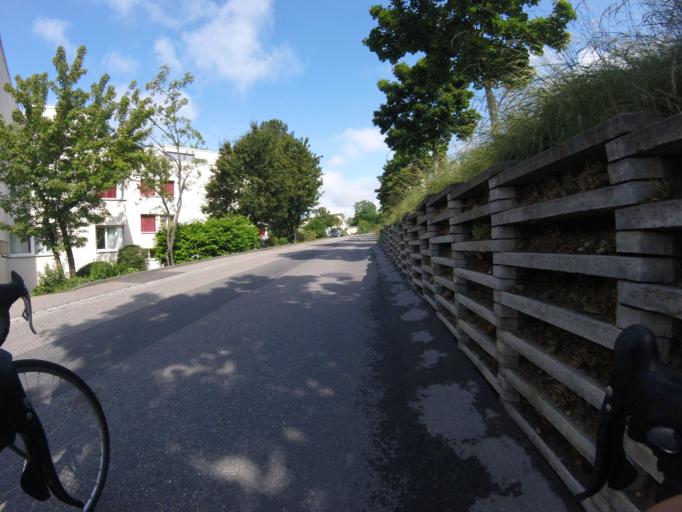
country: CH
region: Bern
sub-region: Bern-Mittelland District
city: Worb
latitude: 46.9287
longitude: 7.5696
